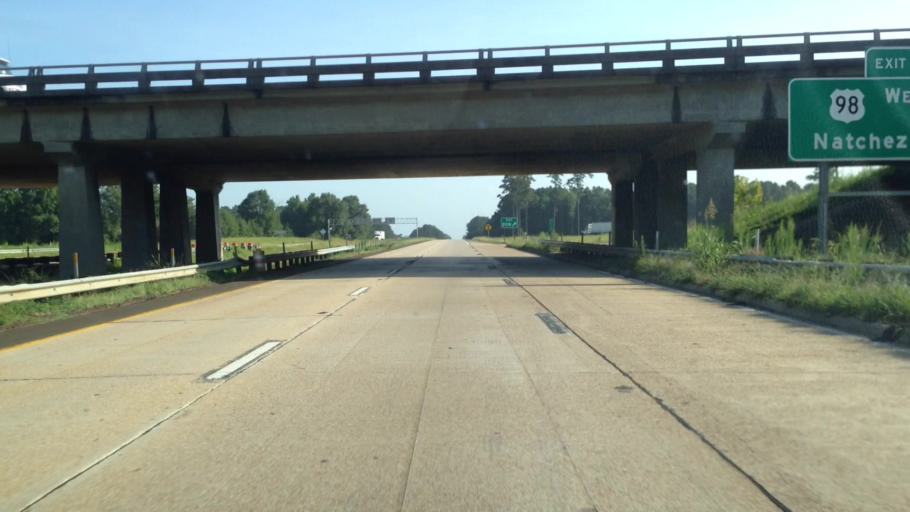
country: US
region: Mississippi
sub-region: Pike County
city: Summit
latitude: 31.2883
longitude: -90.4785
